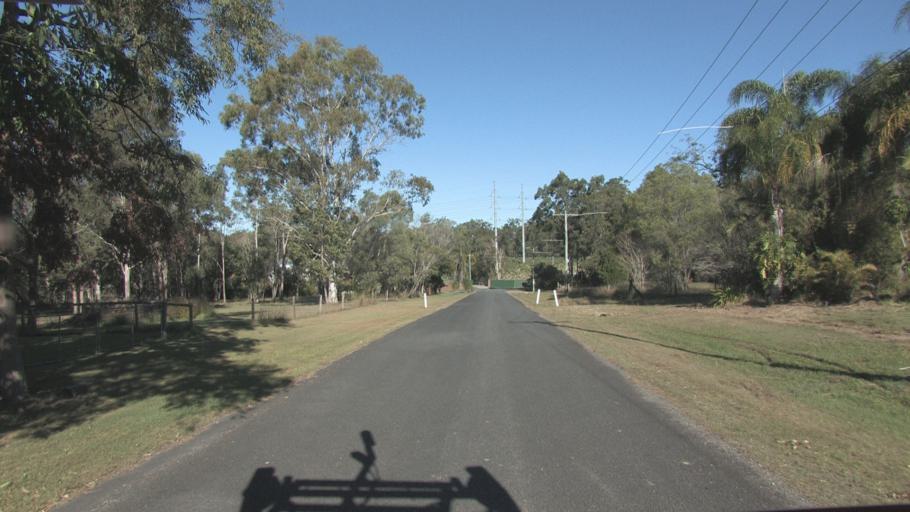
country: AU
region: Queensland
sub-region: Logan
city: Park Ridge South
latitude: -27.7319
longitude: 153.0258
